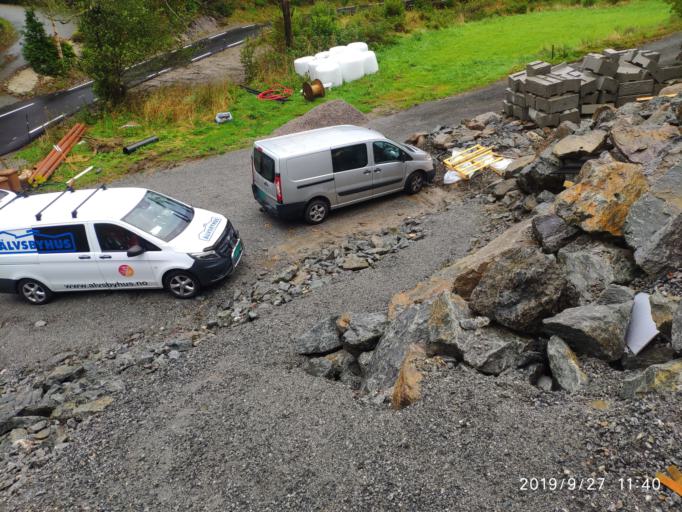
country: NO
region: Rogaland
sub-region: Karmoy
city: Kopervik
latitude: 59.2896
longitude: 5.3632
